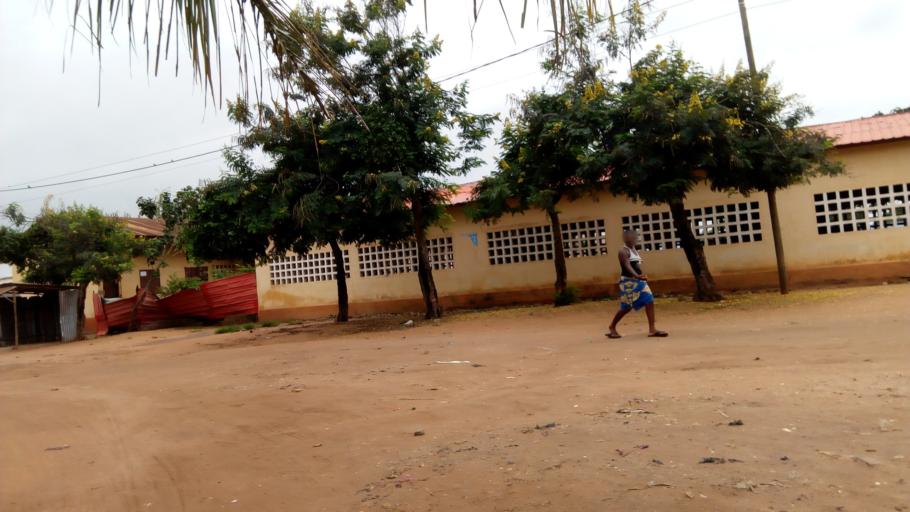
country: TG
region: Maritime
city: Lome
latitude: 6.1784
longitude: 1.1794
